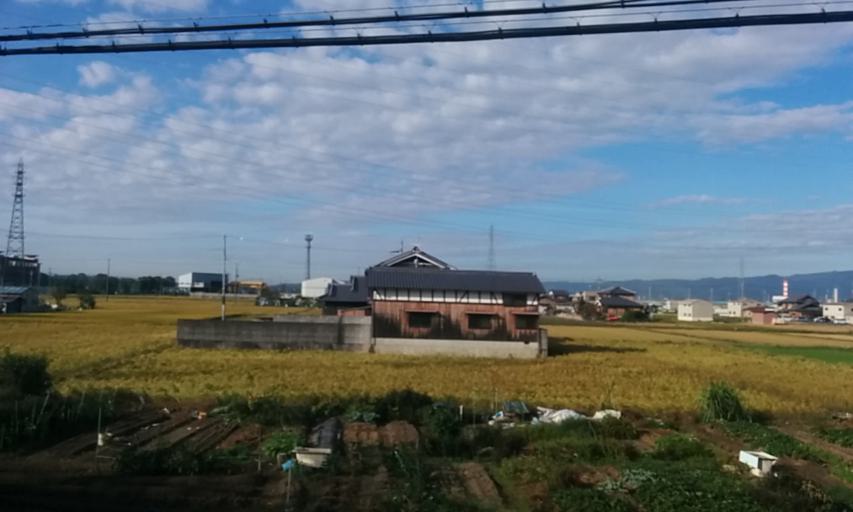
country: JP
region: Kyoto
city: Uji
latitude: 34.9173
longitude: 135.7683
